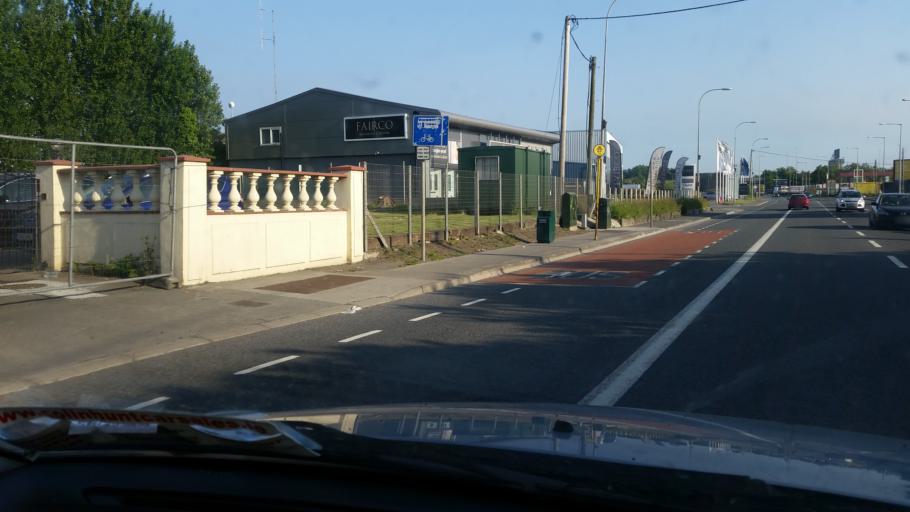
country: IE
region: Leinster
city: Beaumont
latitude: 53.4138
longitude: -6.2390
